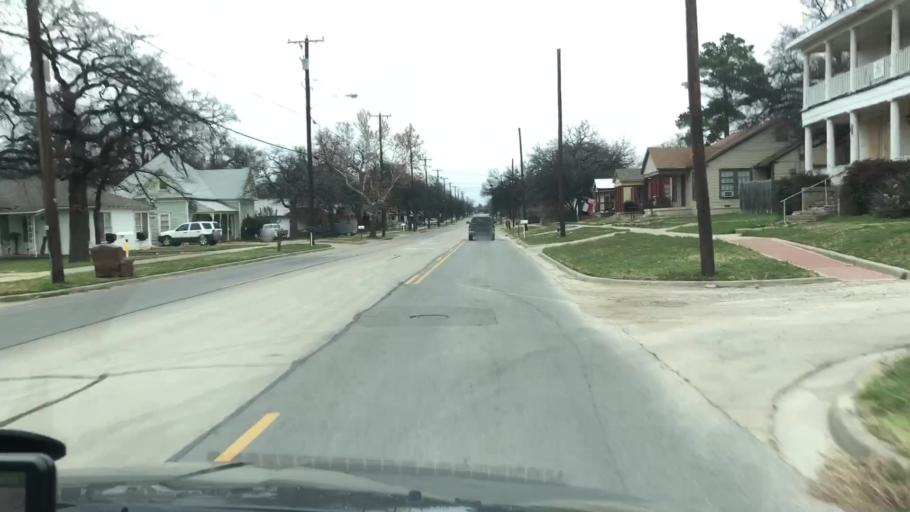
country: US
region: Texas
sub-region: Palo Pinto County
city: Mineral Wells
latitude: 32.8174
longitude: -98.1129
